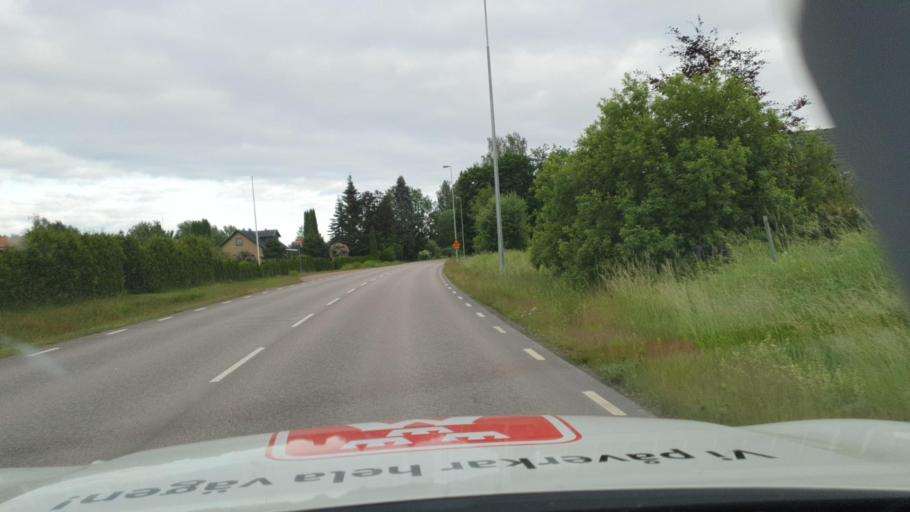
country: SE
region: Vaermland
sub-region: Forshaga Kommun
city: Forshaga
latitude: 59.4447
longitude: 13.4405
